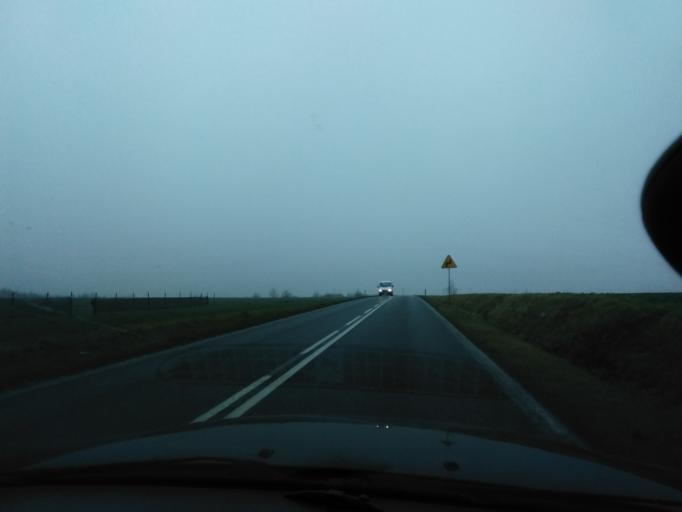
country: PL
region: Subcarpathian Voivodeship
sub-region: Powiat lancucki
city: Sonina
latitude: 50.0506
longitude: 22.2884
